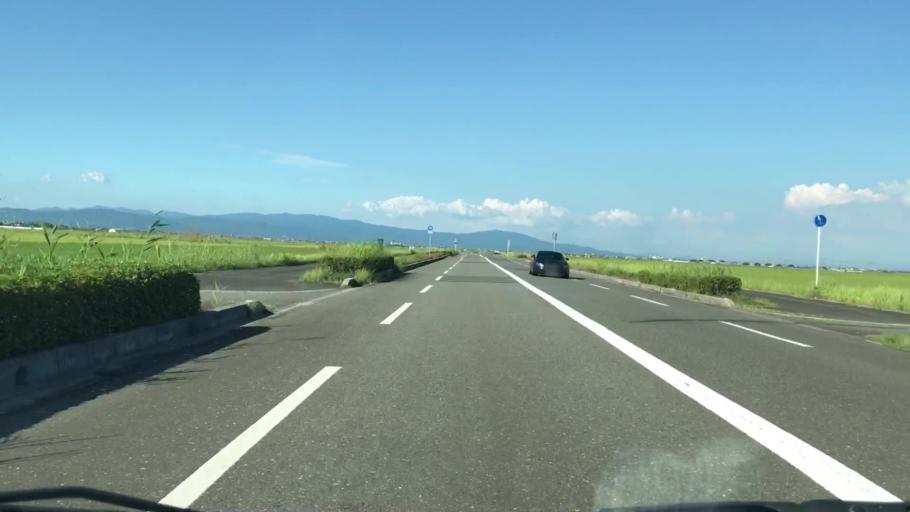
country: JP
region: Saga Prefecture
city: Okawa
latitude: 33.1637
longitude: 130.2912
